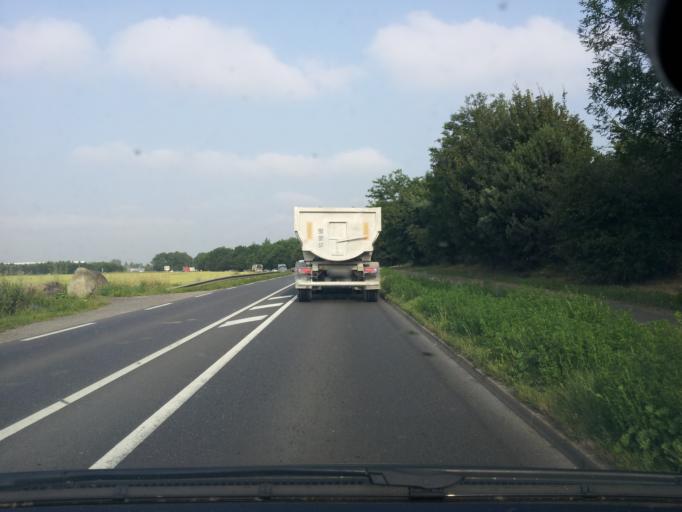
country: FR
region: Ile-de-France
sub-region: Departement de l'Essonne
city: Bondoufle
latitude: 48.6030
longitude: 2.3802
